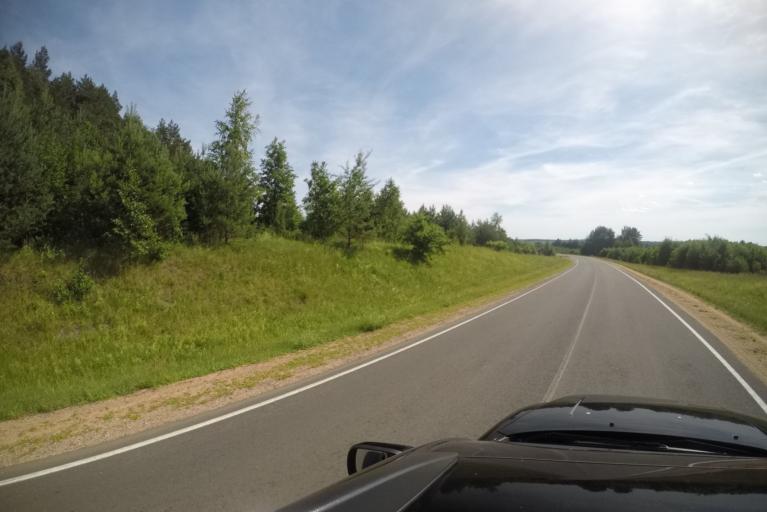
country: BY
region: Grodnenskaya
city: Hal'shany
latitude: 54.2732
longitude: 26.0333
